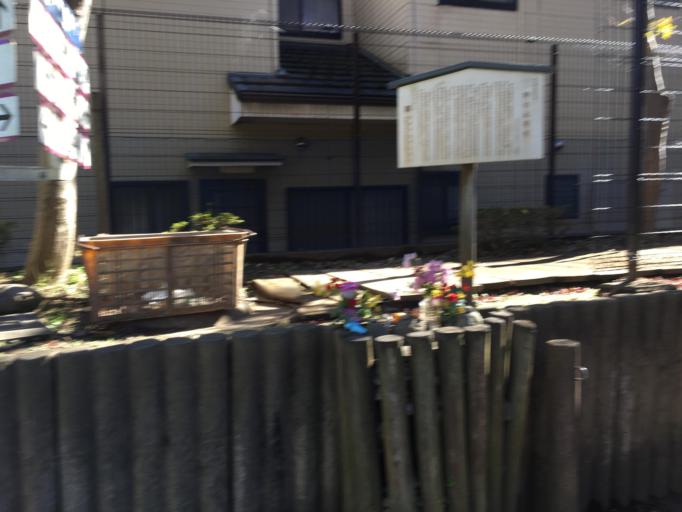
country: JP
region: Saitama
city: Asaka
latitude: 35.7881
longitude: 139.5571
